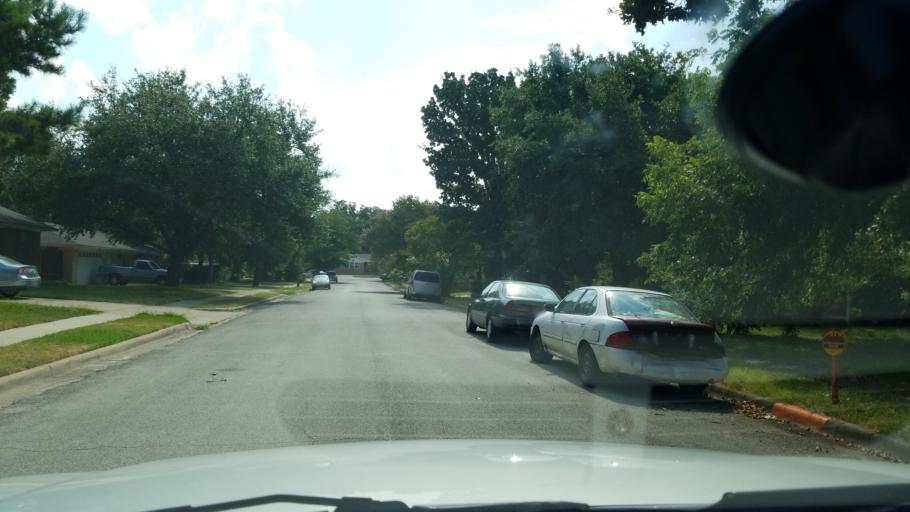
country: US
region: Texas
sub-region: Dallas County
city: Irving
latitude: 32.8328
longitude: -96.9269
